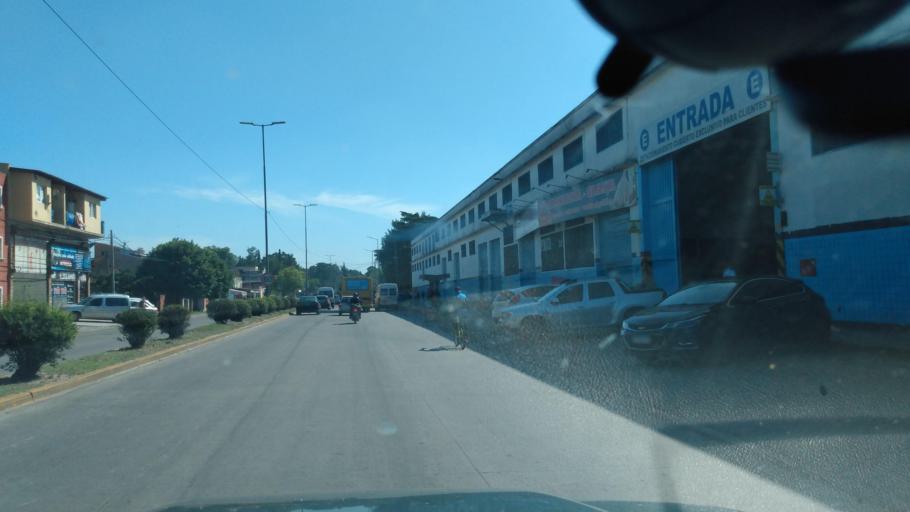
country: AR
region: Buenos Aires
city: Hurlingham
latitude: -34.5538
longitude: -58.7244
